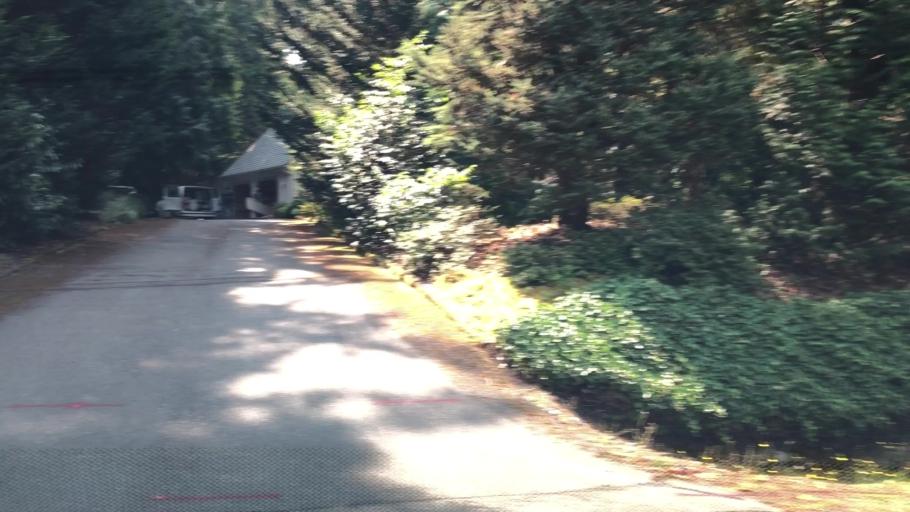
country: US
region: Washington
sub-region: King County
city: Cottage Lake
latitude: 47.7702
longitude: -122.0790
